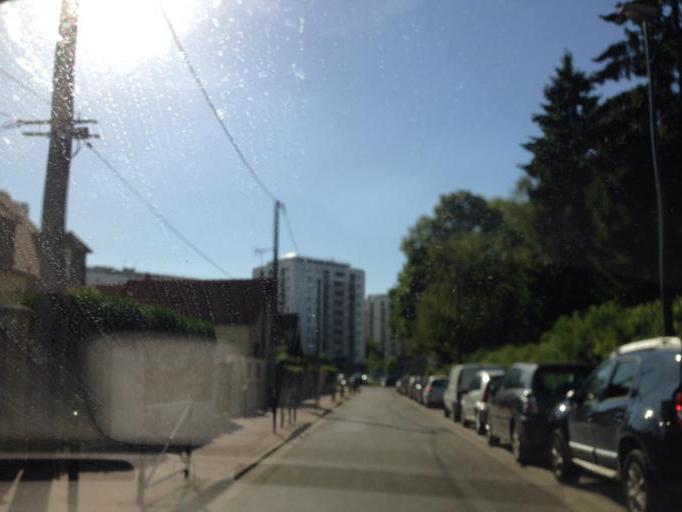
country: FR
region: Ile-de-France
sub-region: Departement des Hauts-de-Seine
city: Meudon
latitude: 48.7860
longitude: 2.2388
